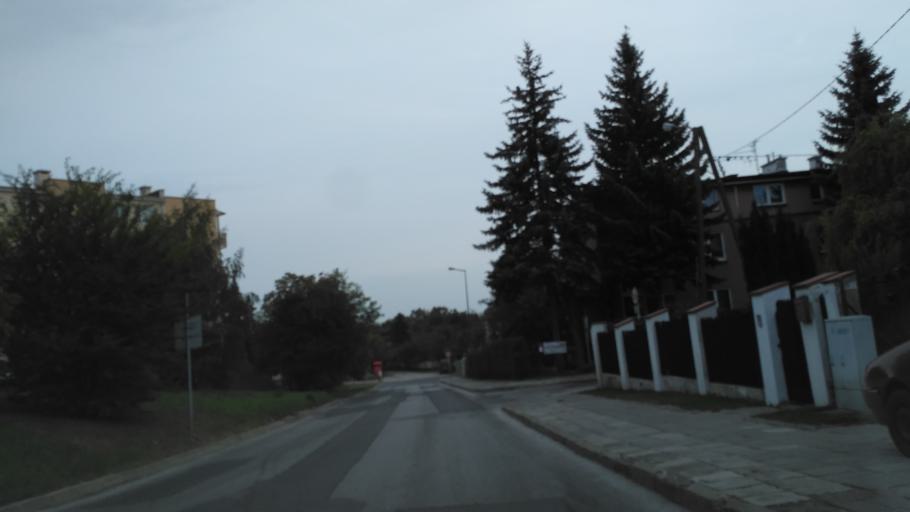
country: PL
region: Lublin Voivodeship
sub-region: Powiat lubelski
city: Lublin
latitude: 51.2265
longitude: 22.5936
